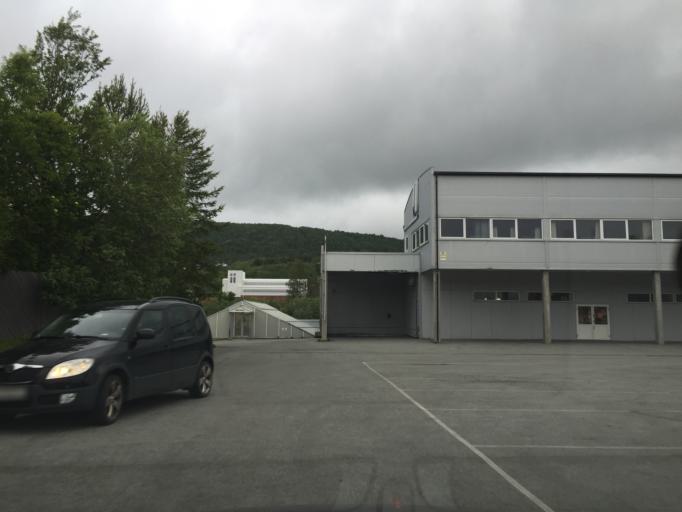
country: NO
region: Nordland
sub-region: Bodo
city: Lopsmarka
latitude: 67.2804
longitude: 14.5449
